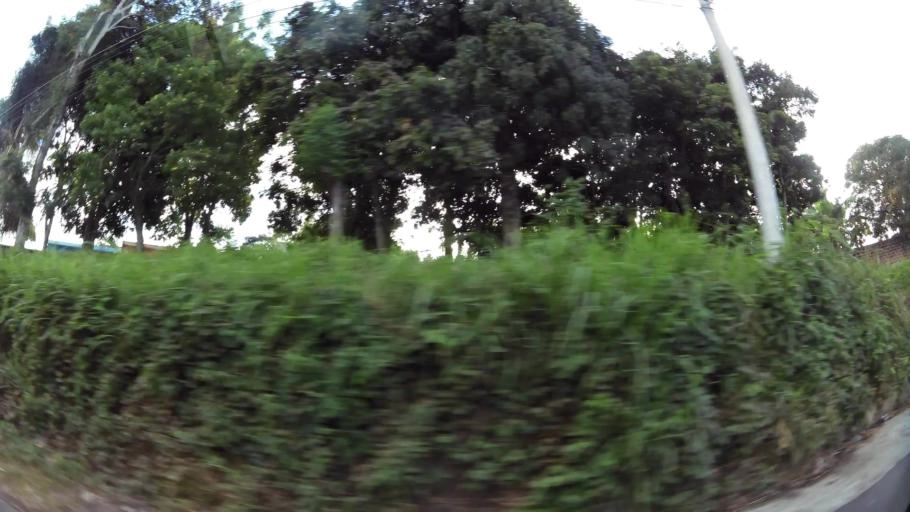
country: SV
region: Cuscatlan
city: Cojutepeque
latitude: 13.7174
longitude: -88.9275
